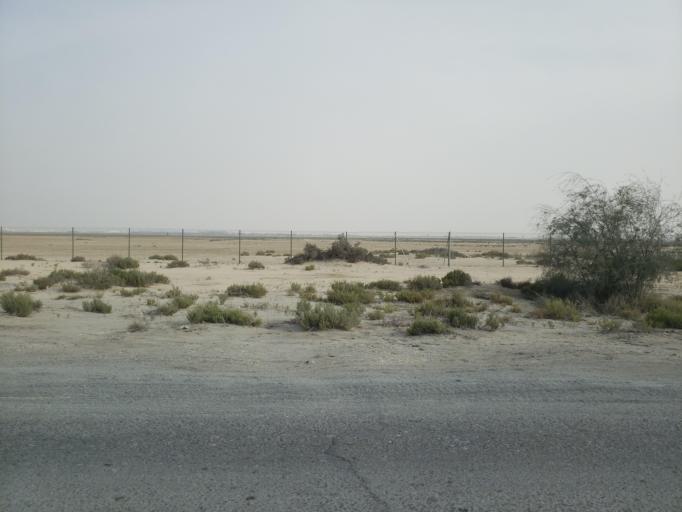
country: AE
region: Dubai
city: Dubai
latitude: 24.9596
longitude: 55.0210
